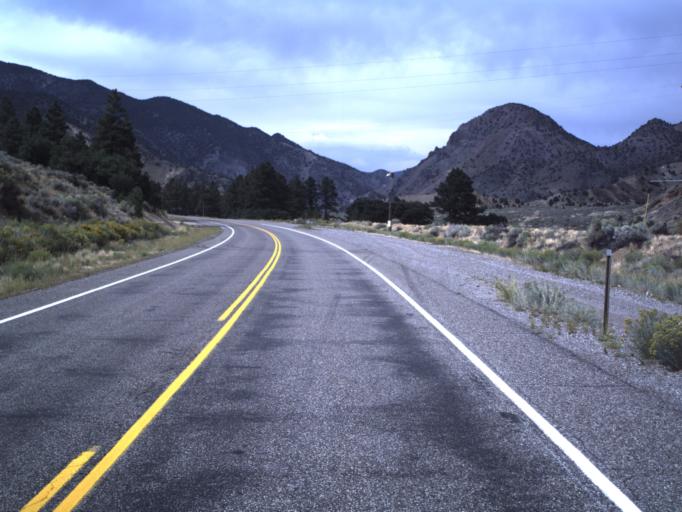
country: US
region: Utah
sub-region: Sevier County
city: Monroe
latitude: 38.5091
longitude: -112.2599
